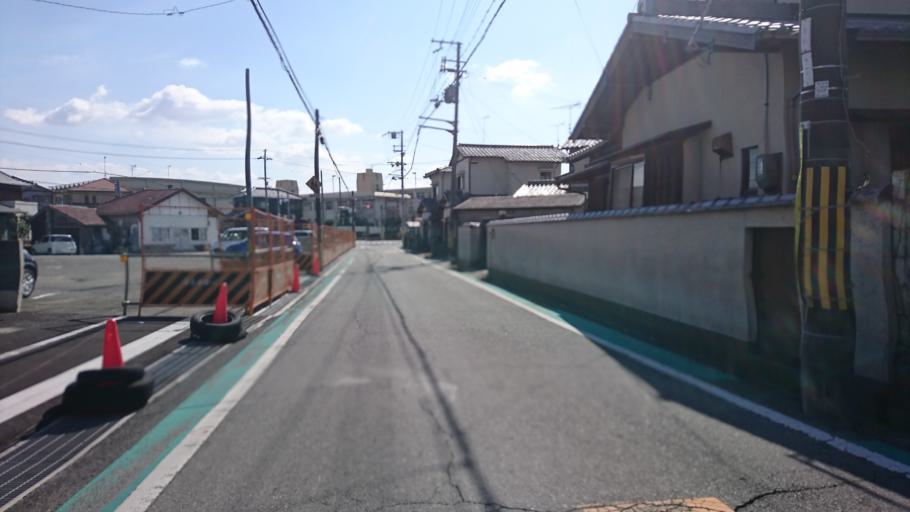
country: JP
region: Hyogo
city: Kakogawacho-honmachi
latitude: 34.8201
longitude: 134.8213
